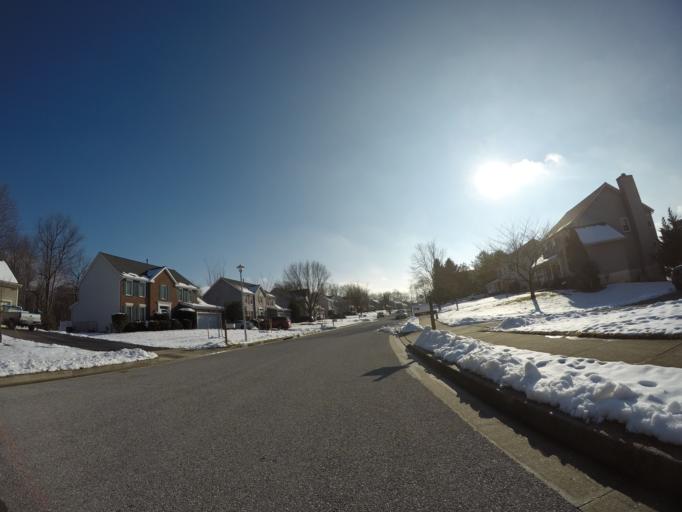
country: US
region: Maryland
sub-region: Howard County
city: Ilchester
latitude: 39.2176
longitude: -76.7755
